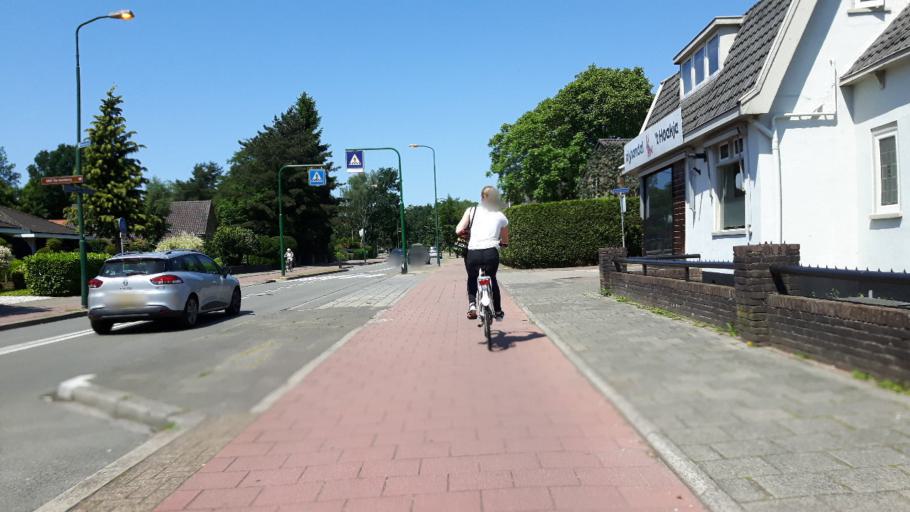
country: NL
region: Utrecht
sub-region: Gemeente Soest
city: Soest
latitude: 52.1725
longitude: 5.2935
